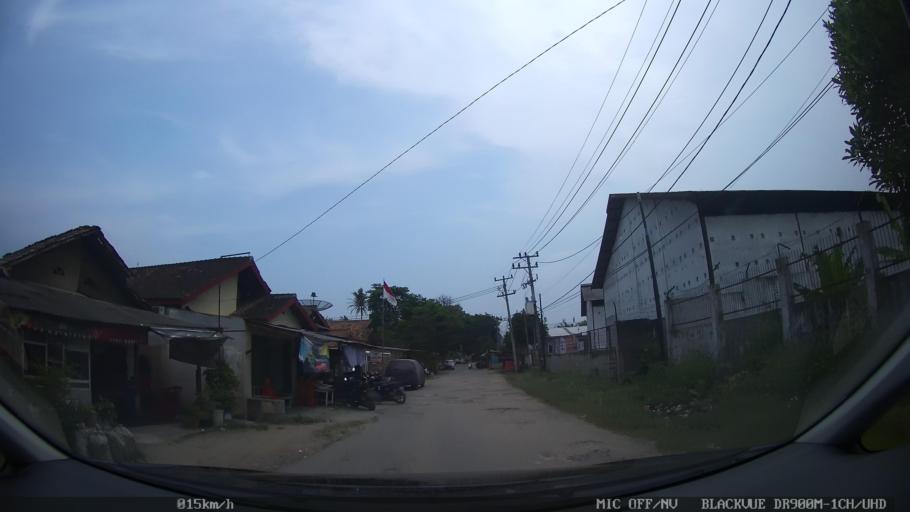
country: ID
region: Lampung
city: Panjang
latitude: -5.4332
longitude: 105.3272
